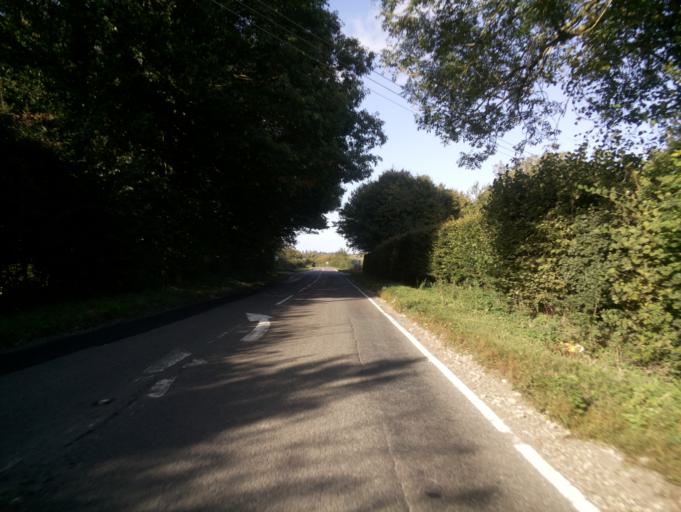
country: GB
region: England
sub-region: Hampshire
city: Alton
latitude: 51.0989
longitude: -0.9942
